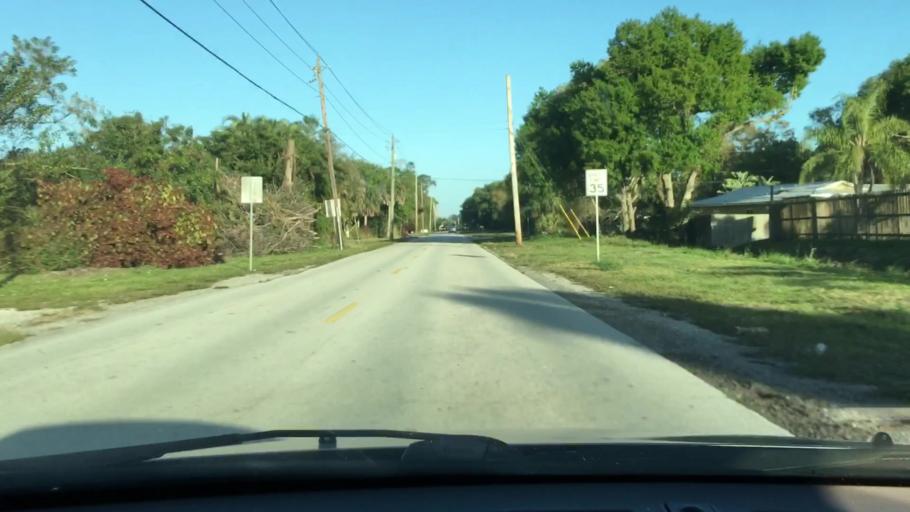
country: US
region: Florida
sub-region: Indian River County
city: Vero Beach South
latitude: 27.6461
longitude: -80.4387
